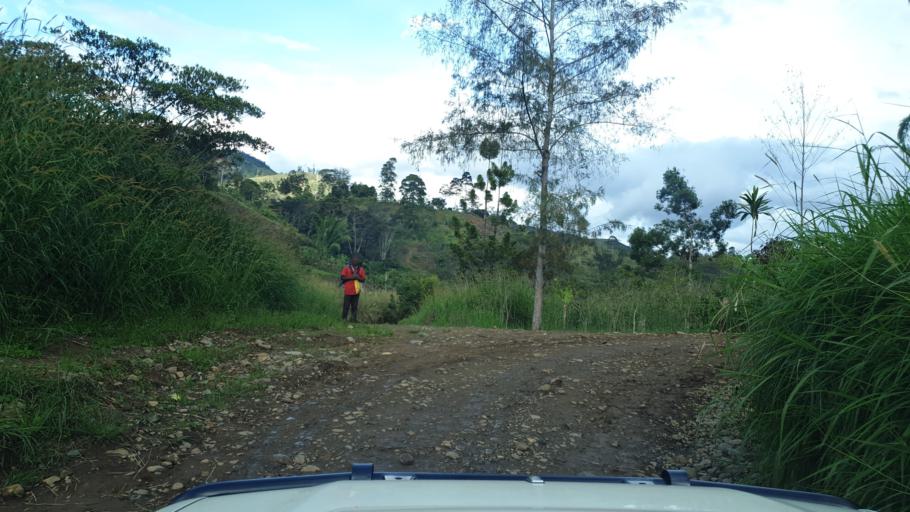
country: PG
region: Eastern Highlands
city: Goroka
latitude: -5.9354
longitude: 145.2669
